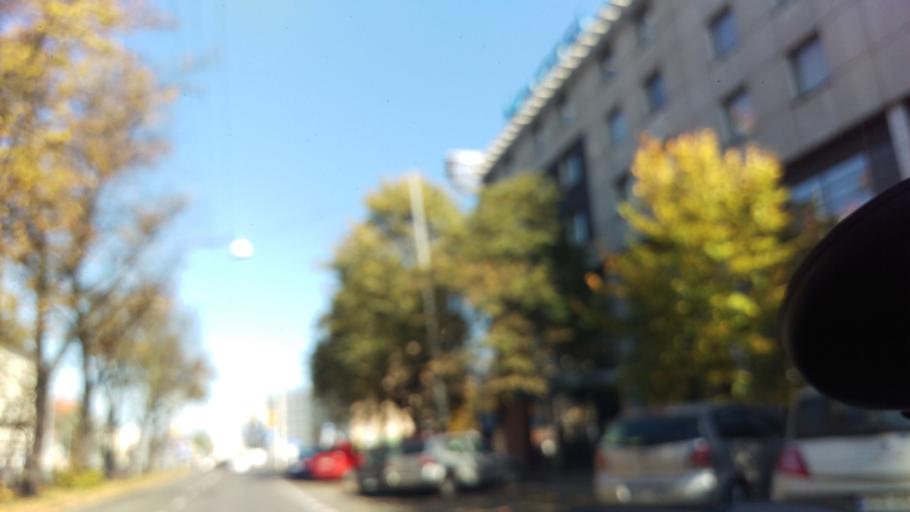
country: PL
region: West Pomeranian Voivodeship
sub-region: Szczecin
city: Szczecin
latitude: 53.4230
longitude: 14.5505
